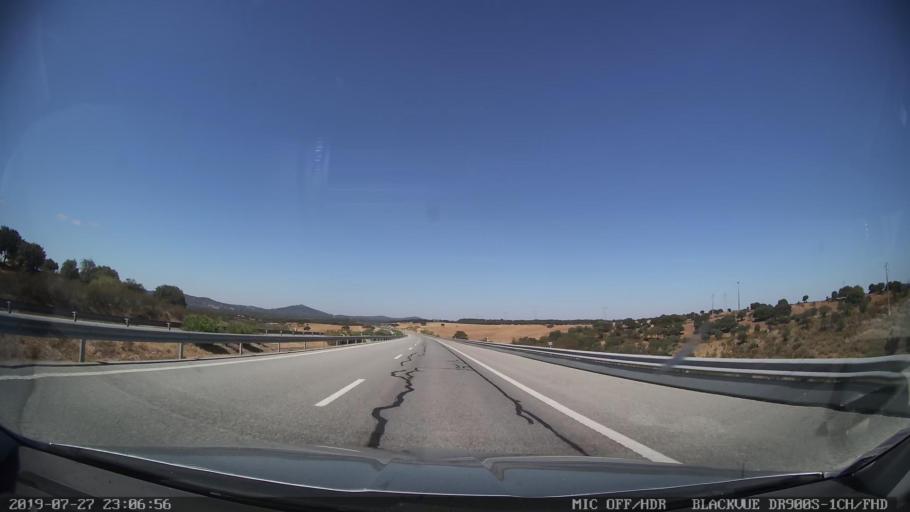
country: PT
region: Evora
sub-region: Estremoz
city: Estremoz
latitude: 38.8065
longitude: -7.6420
